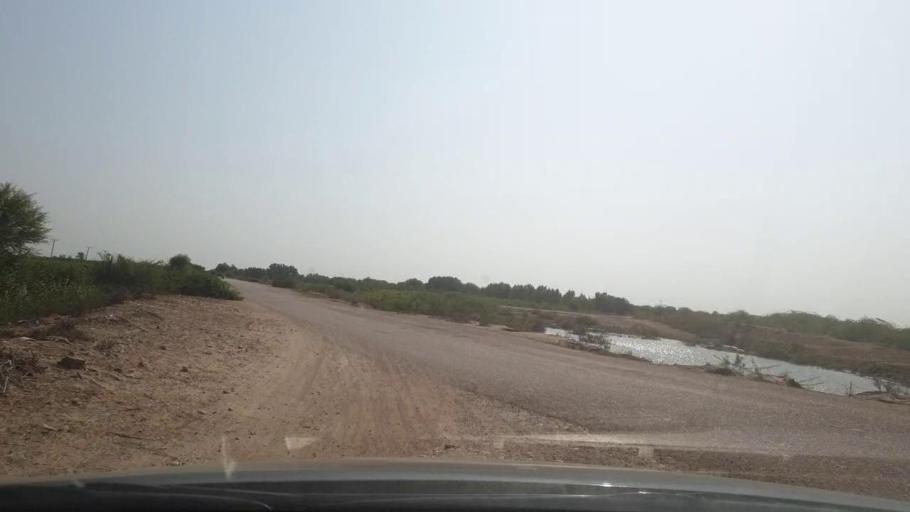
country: PK
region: Sindh
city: Naukot
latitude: 24.7900
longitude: 69.2076
